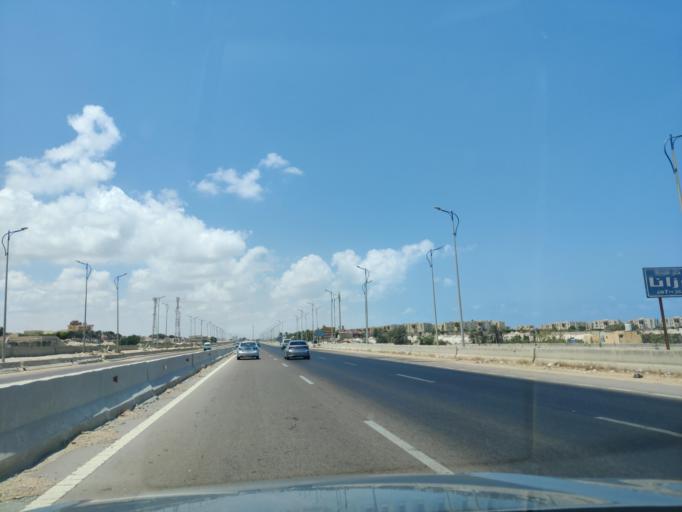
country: EG
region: Muhafazat Matruh
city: Al `Alamayn
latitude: 30.9141
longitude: 29.4441
